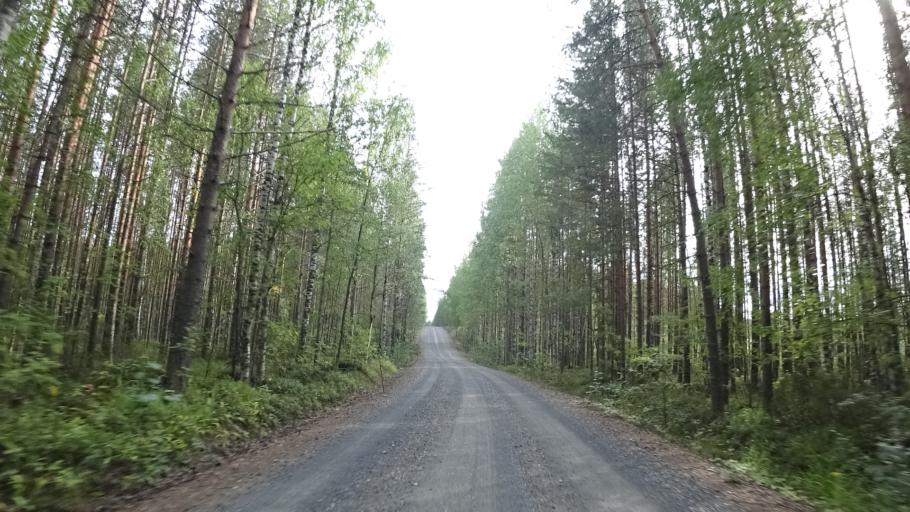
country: FI
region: North Karelia
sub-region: Joensuu
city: Ilomantsi
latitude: 62.6094
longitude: 31.1854
